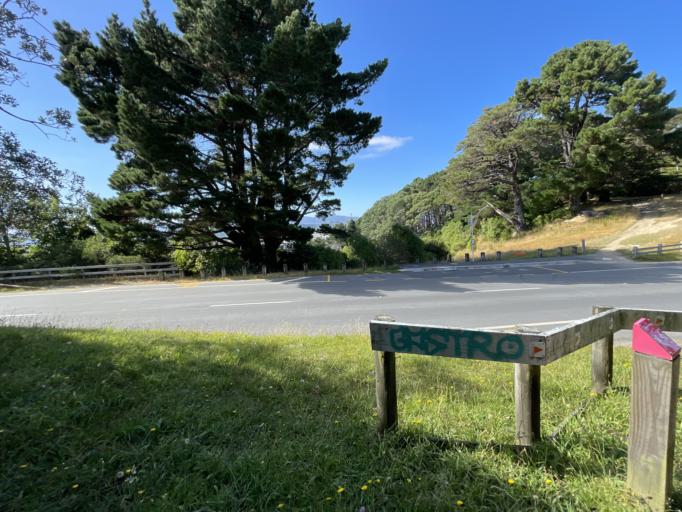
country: NZ
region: Wellington
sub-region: Wellington City
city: Wellington
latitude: -41.3068
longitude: 174.7882
